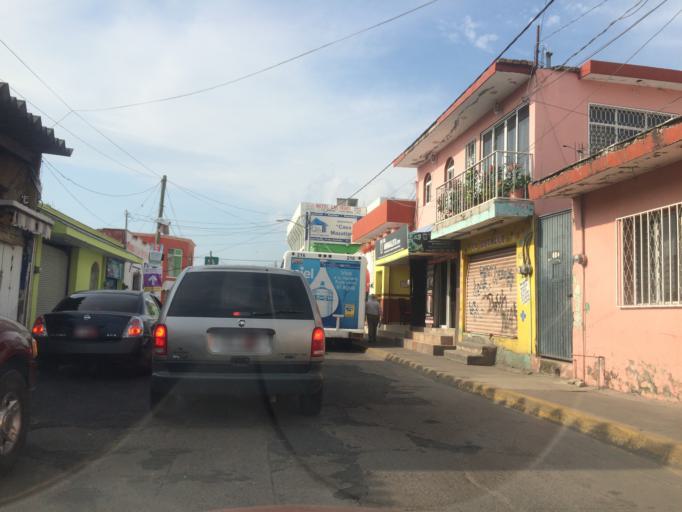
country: MX
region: Nayarit
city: Xalisco
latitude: 21.4475
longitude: -104.8996
